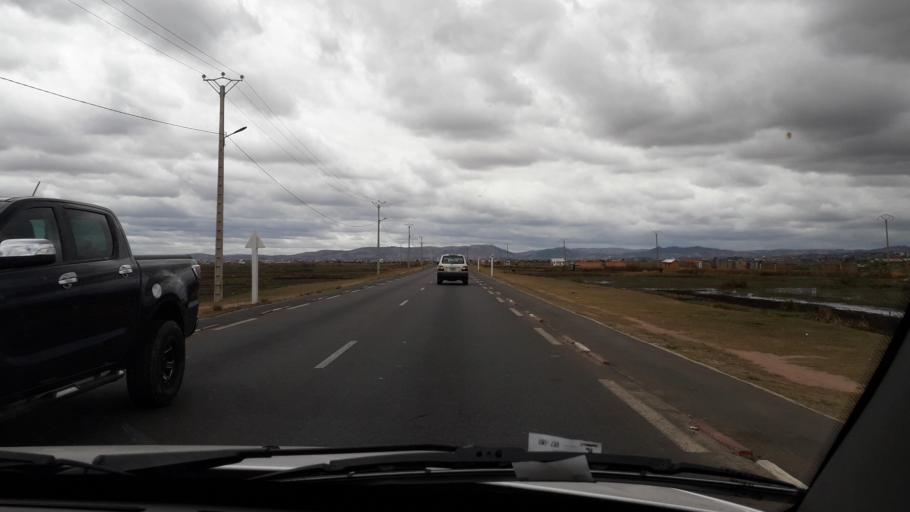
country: MG
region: Analamanga
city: Antananarivo
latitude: -18.8471
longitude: 47.5137
